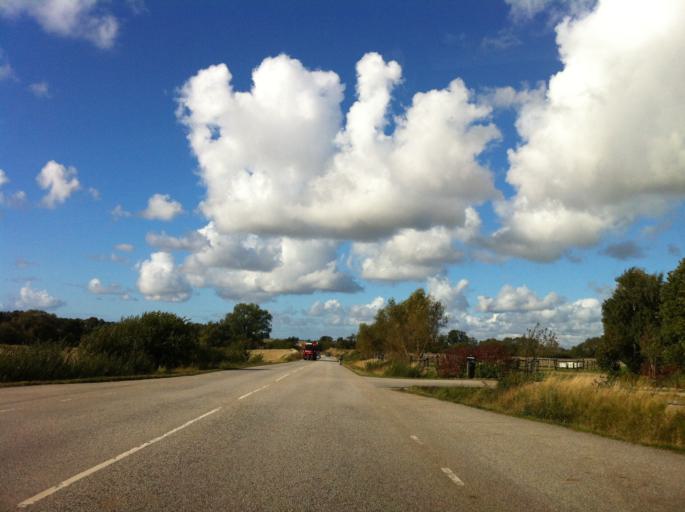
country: SE
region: Skane
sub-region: Kavlinge Kommun
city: Loddekopinge
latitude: 55.8181
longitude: 13.0394
